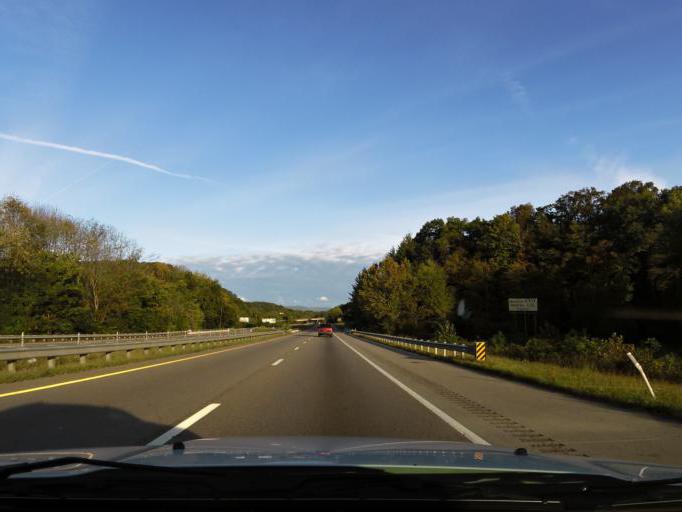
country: US
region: Tennessee
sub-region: Anderson County
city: Norris
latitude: 36.1415
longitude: -84.0475
